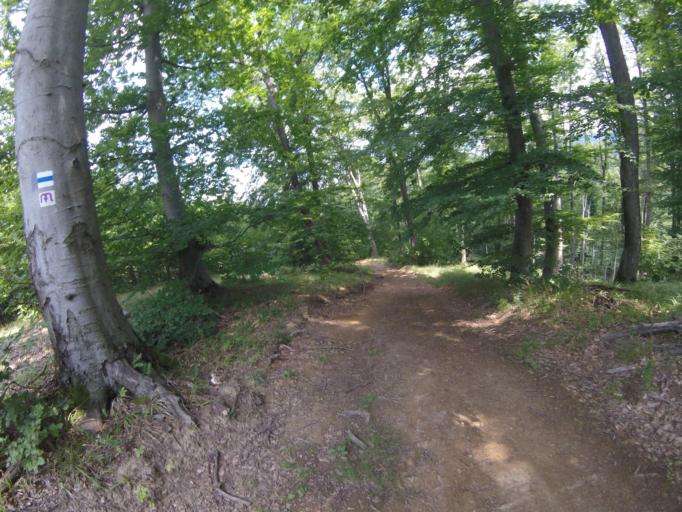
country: SK
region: Nitriansky
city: Sahy
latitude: 47.9536
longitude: 18.8944
